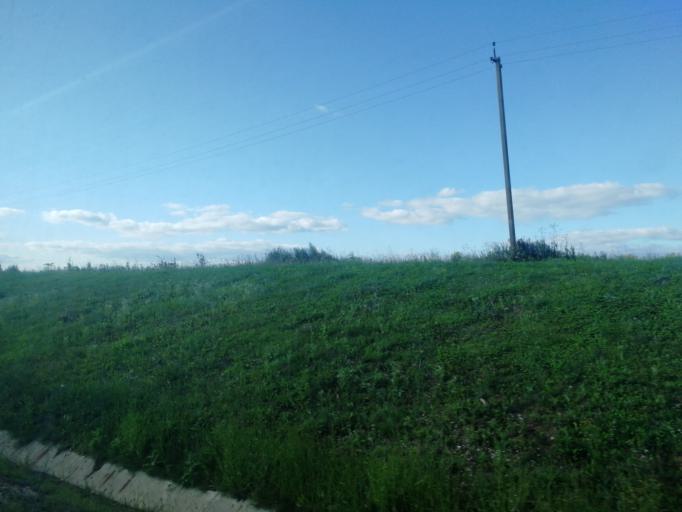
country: RU
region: Tula
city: Leninskiy
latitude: 54.2398
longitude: 37.3415
